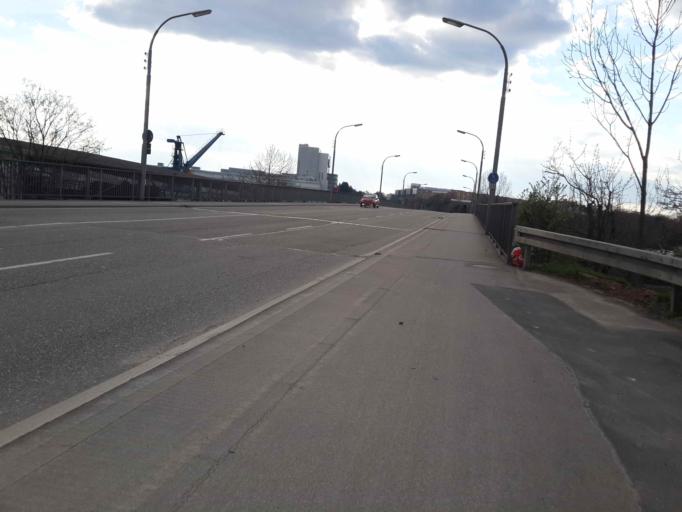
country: DE
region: Baden-Wuerttemberg
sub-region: Regierungsbezirk Stuttgart
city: Heilbronn
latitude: 49.1519
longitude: 9.2051
